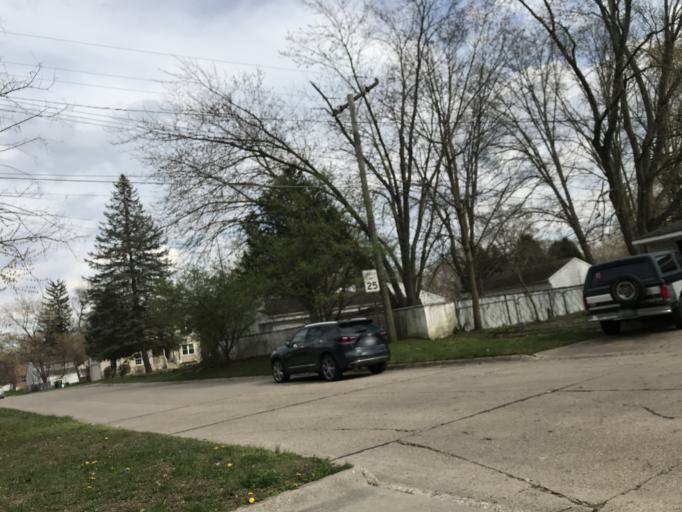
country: US
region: Michigan
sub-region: Oakland County
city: Farmington
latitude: 42.4605
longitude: -83.3422
